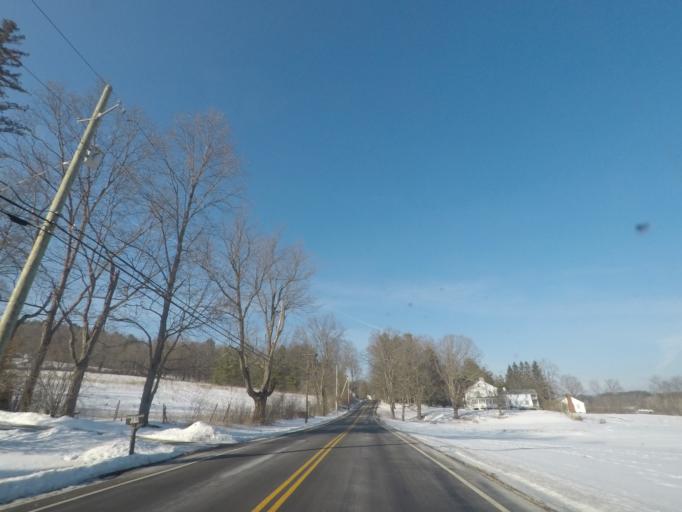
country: US
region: Massachusetts
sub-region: Berkshire County
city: Richmond
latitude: 42.4768
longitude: -73.3902
